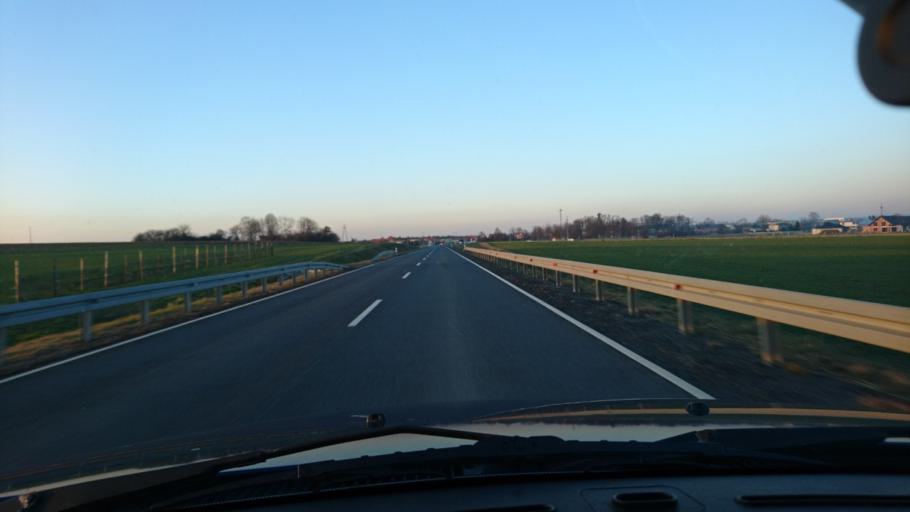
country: PL
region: Silesian Voivodeship
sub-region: Powiat gliwicki
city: Wielowies
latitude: 50.4997
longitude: 18.6058
